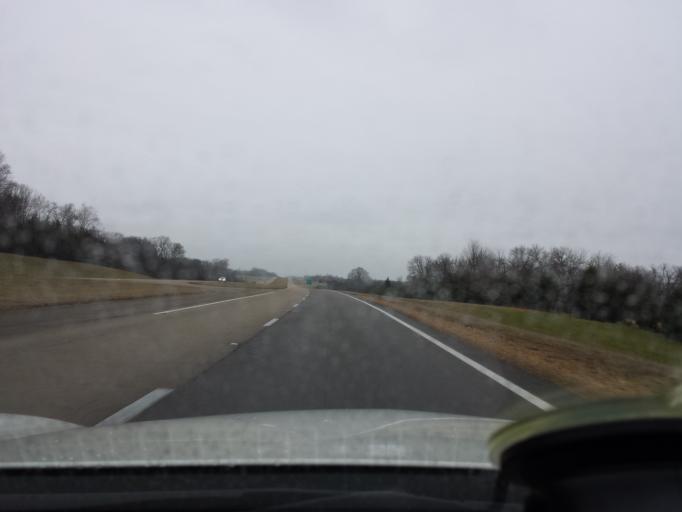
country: US
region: Mississippi
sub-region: Chickasaw County
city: Okolona
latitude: 33.9903
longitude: -88.7014
